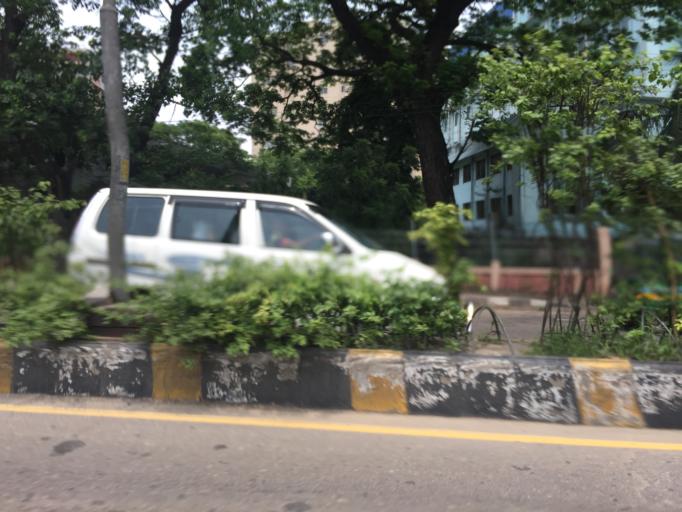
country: BD
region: Dhaka
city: Paltan
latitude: 23.7312
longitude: 90.4047
